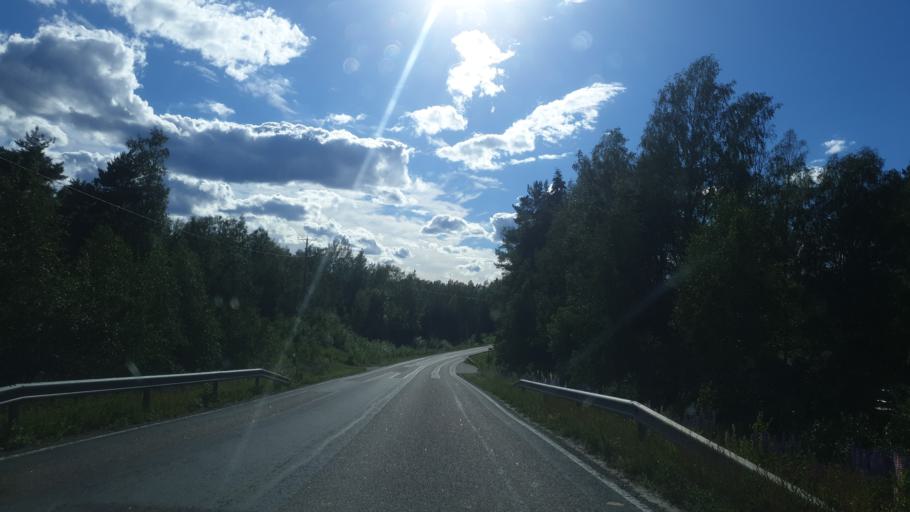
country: FI
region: Southern Savonia
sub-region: Mikkeli
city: Pertunmaa
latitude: 61.5256
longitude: 26.6286
